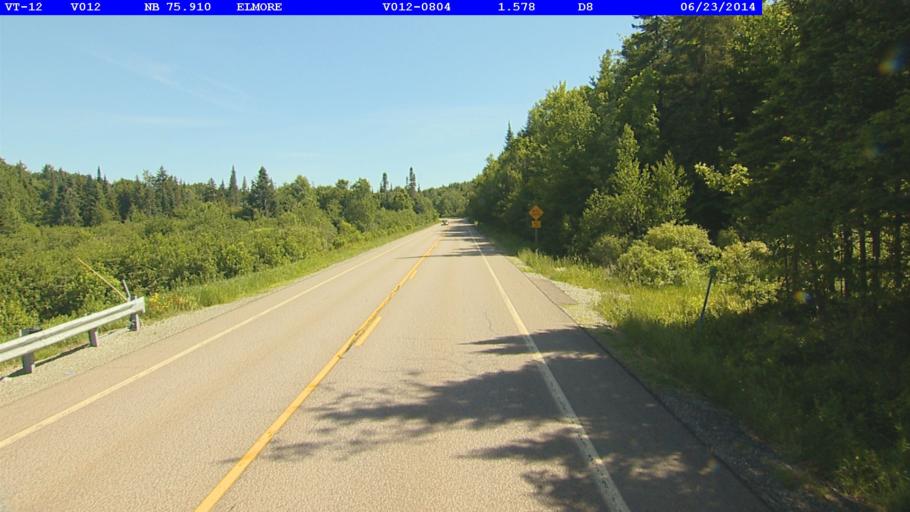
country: US
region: Vermont
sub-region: Lamoille County
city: Morrisville
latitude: 44.4703
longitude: -72.5327
